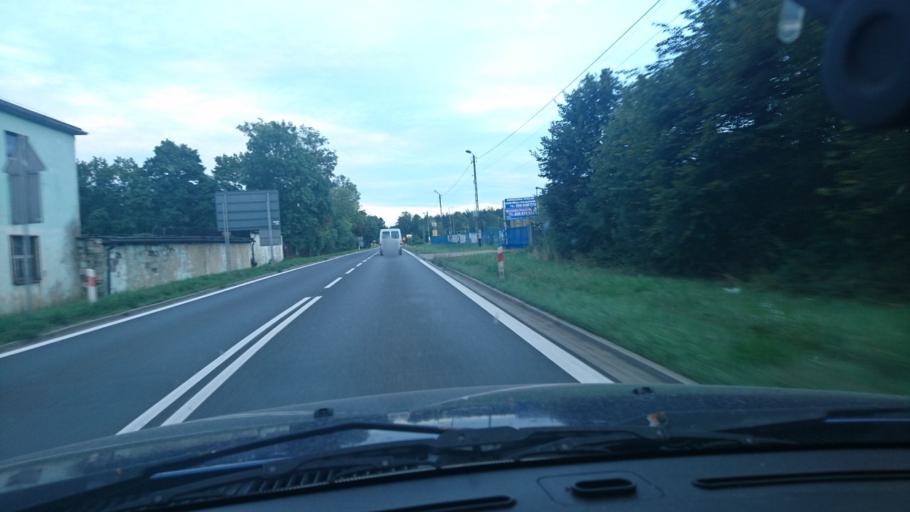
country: PL
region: Silesian Voivodeship
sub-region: Powiat tarnogorski
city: Tworog
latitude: 50.5279
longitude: 18.7175
